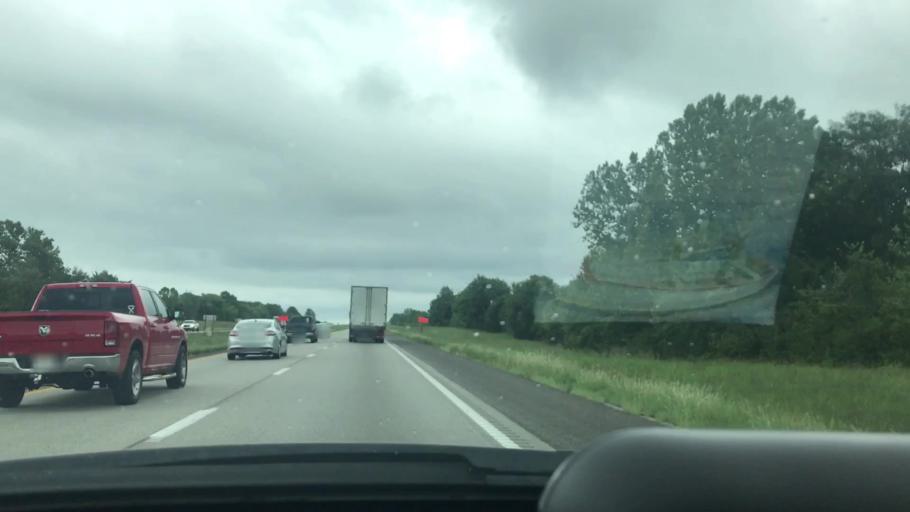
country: US
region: Missouri
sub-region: Christian County
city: Billings
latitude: 37.1862
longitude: -93.6036
